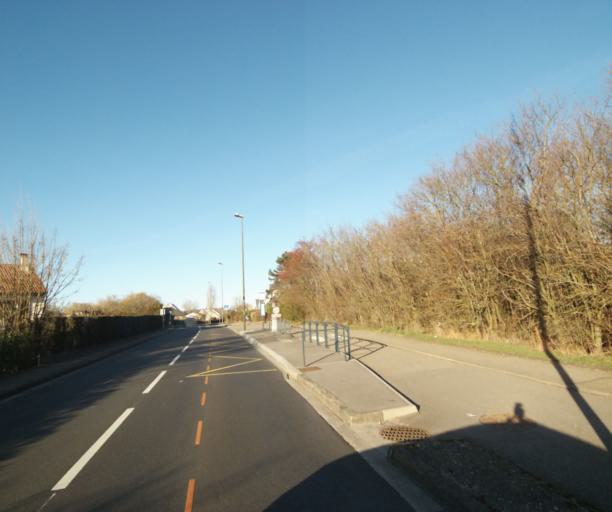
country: FR
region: Lorraine
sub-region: Departement de Meurthe-et-Moselle
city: Seichamps
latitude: 48.7090
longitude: 6.2639
